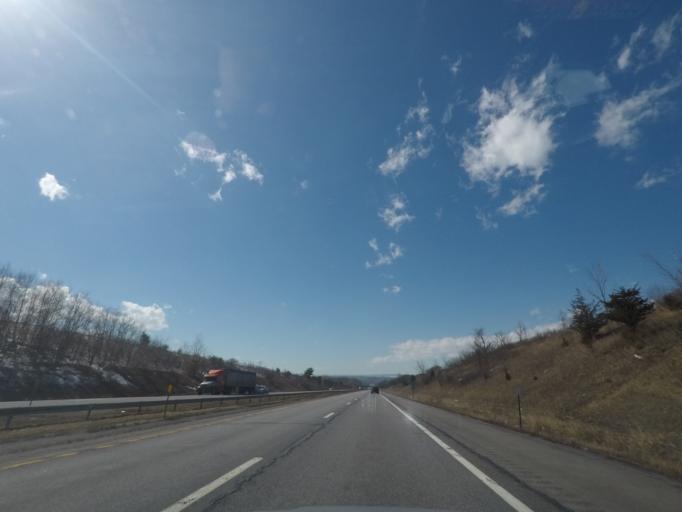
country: US
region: New York
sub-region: Montgomery County
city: Tribes Hill
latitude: 42.9328
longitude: -74.2611
